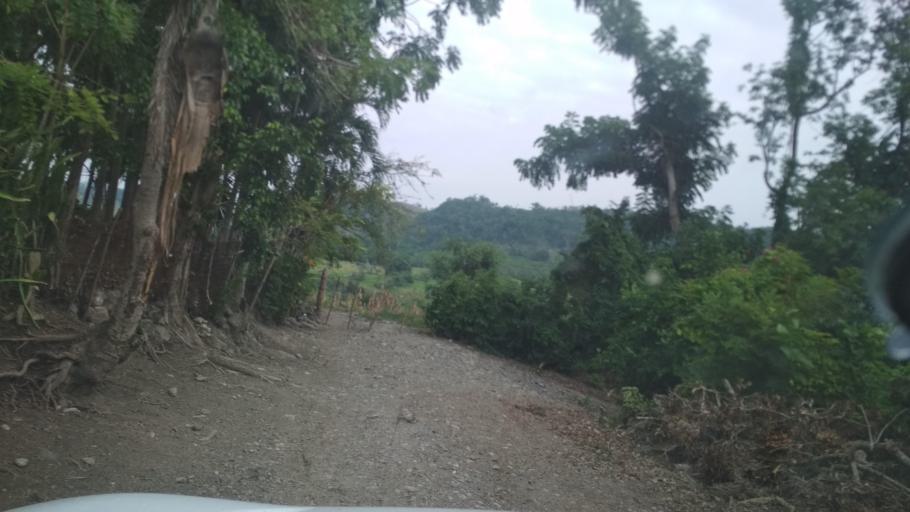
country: MX
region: Veracruz
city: Papantla de Olarte
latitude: 20.5130
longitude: -97.3369
